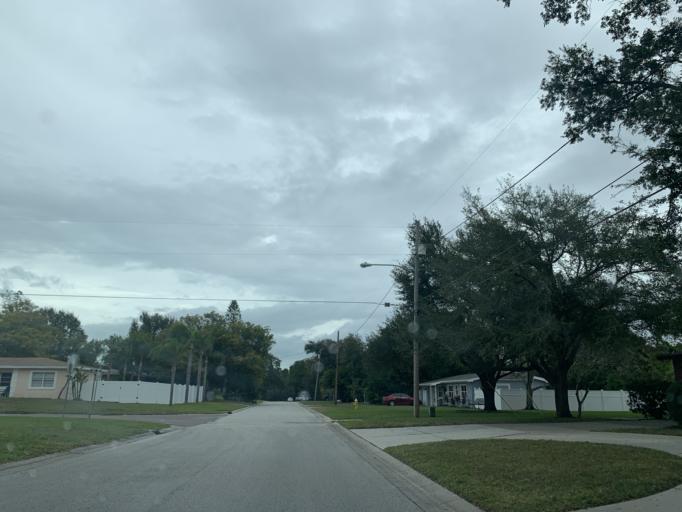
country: US
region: Florida
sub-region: Pinellas County
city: Belleair
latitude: 27.9368
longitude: -82.8008
